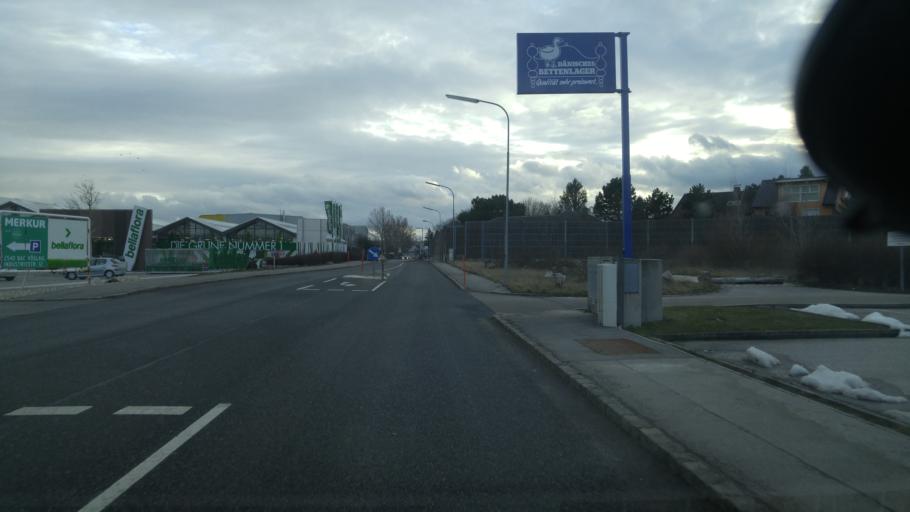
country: AT
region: Lower Austria
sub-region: Politischer Bezirk Baden
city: Bad Voslau
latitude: 47.9764
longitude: 16.2216
